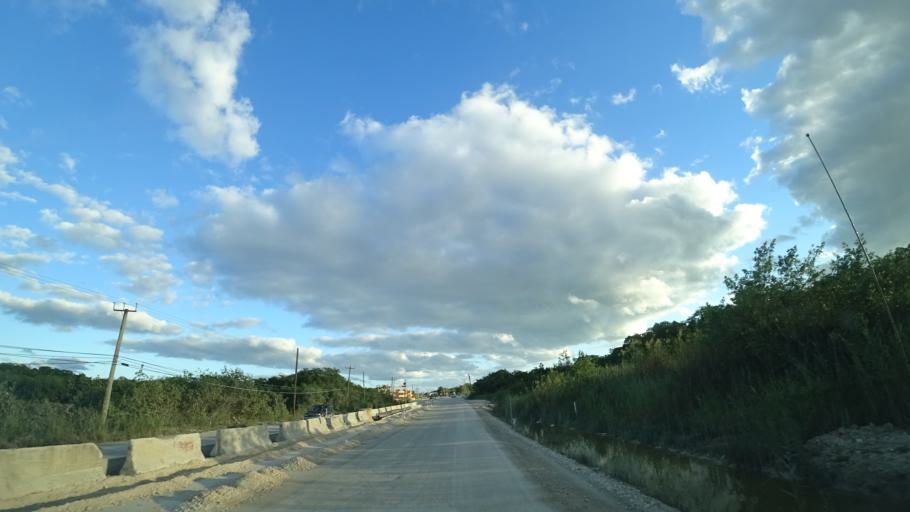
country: BZ
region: Belize
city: Belize City
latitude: 17.5227
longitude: -88.2350
